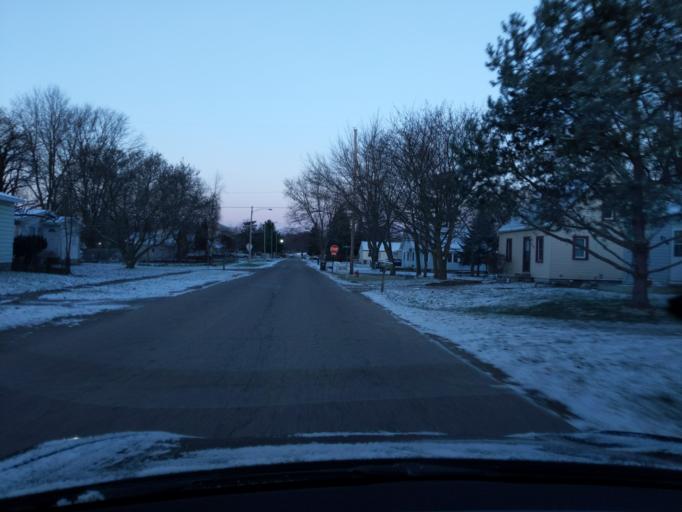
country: US
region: Michigan
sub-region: Ingham County
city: Lansing
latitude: 42.7025
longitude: -84.5642
